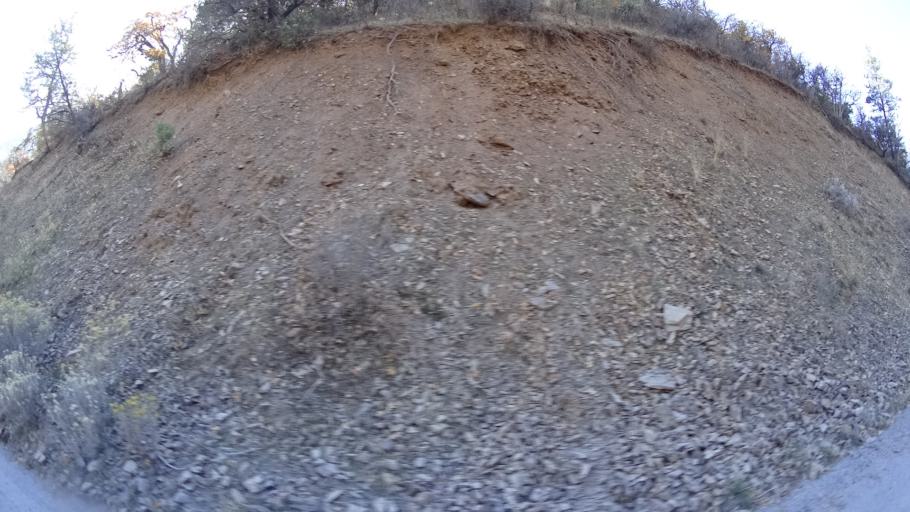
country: US
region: California
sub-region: Siskiyou County
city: Yreka
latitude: 41.8323
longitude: -122.6624
